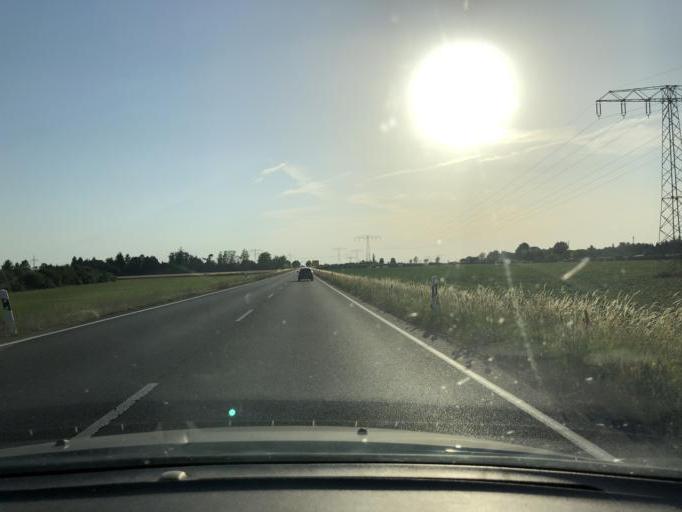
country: DE
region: Saxony
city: Borsdorf
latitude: 51.3549
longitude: 12.5295
